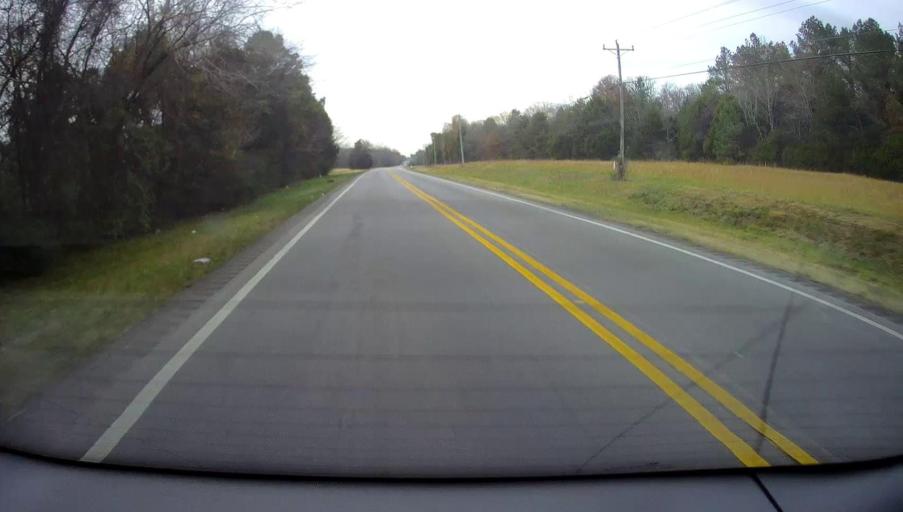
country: US
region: Alabama
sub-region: Morgan County
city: Priceville
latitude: 34.4360
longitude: -86.7402
